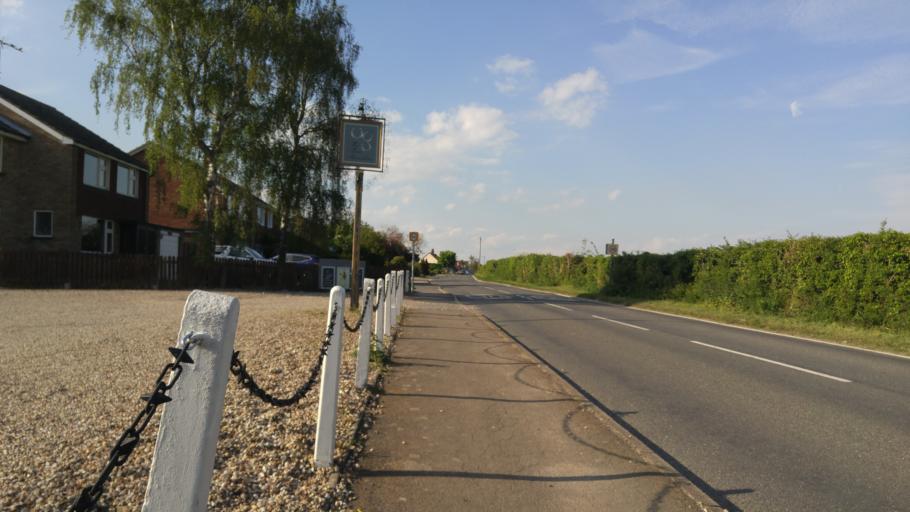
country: GB
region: England
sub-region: Essex
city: Eight Ash Green
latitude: 51.9184
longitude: 0.8021
